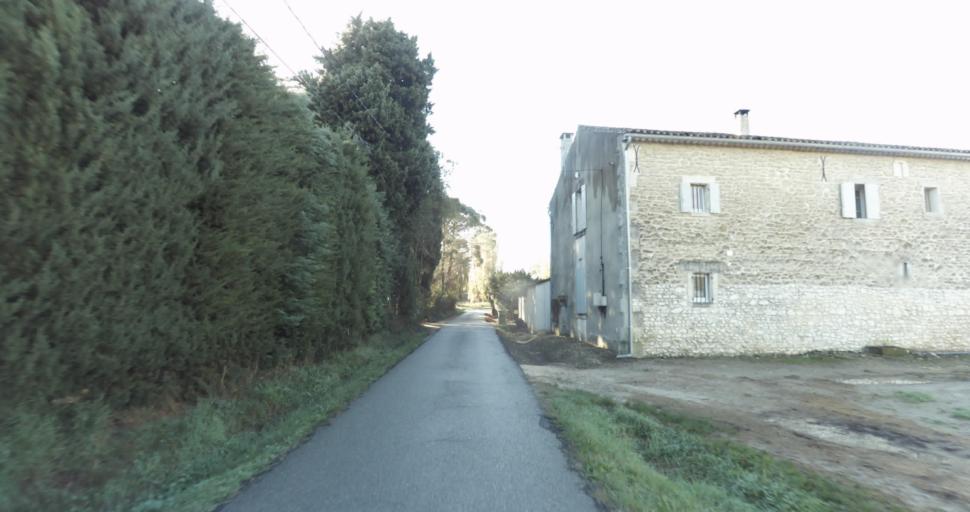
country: FR
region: Provence-Alpes-Cote d'Azur
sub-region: Departement des Bouches-du-Rhone
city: Rognonas
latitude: 43.8830
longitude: 4.8034
